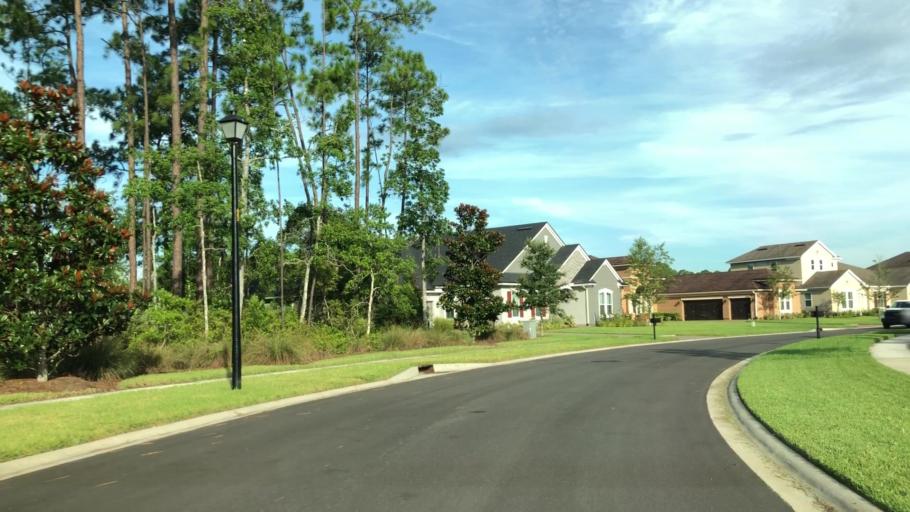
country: US
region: Florida
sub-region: Saint Johns County
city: Palm Valley
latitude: 30.1320
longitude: -81.4257
